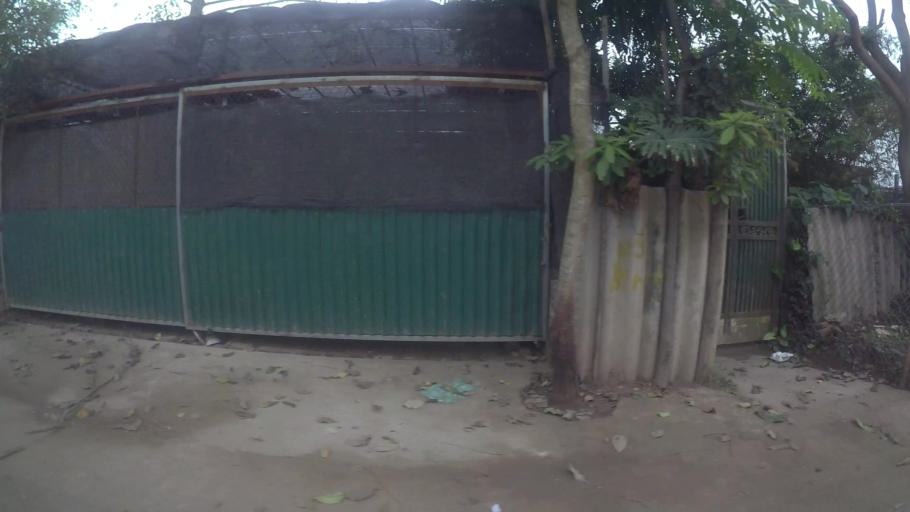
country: VN
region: Ha Noi
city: Tay Ho
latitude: 21.0761
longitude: 105.8255
